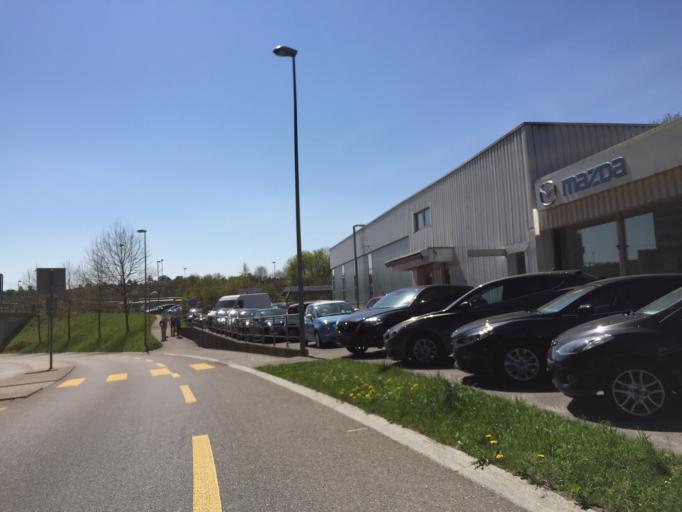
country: CH
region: Bern
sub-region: Bern-Mittelland District
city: Zollikofen
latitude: 46.9802
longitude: 7.4563
